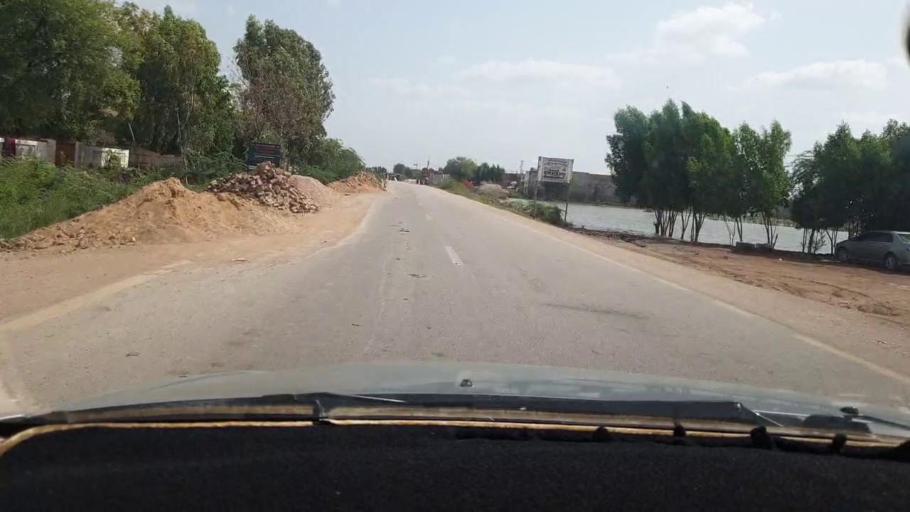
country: PK
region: Sindh
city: Naukot
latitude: 24.9783
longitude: 69.2945
